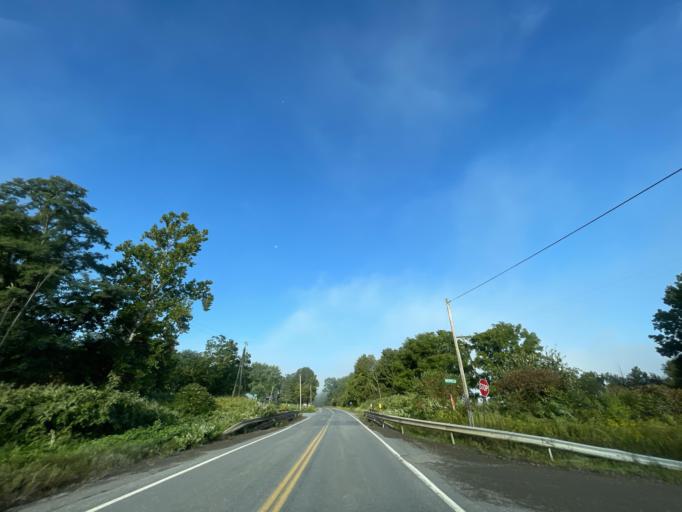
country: US
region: New York
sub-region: Chenango County
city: Oxford
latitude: 42.3678
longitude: -75.6497
